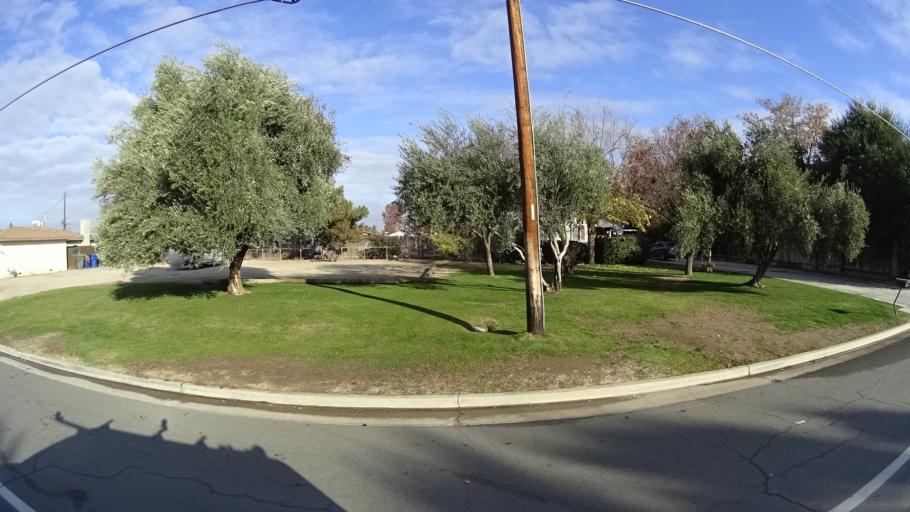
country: US
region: California
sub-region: Kern County
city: Greenfield
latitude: 35.3032
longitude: -119.0488
